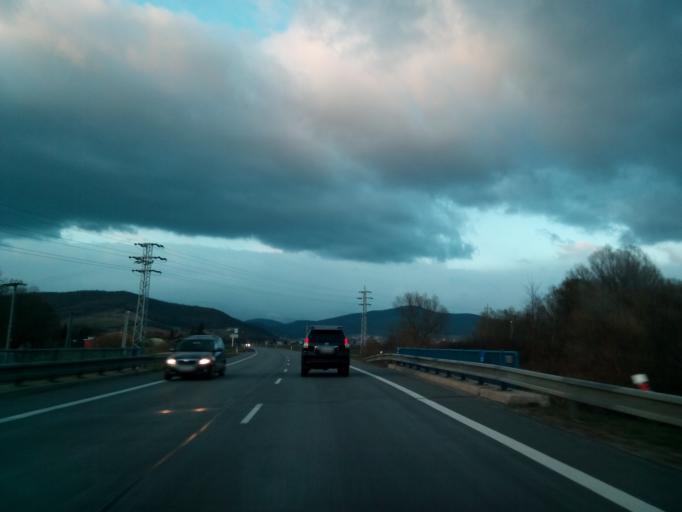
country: SK
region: Kosicky
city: Roznava
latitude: 48.6269
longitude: 20.5014
